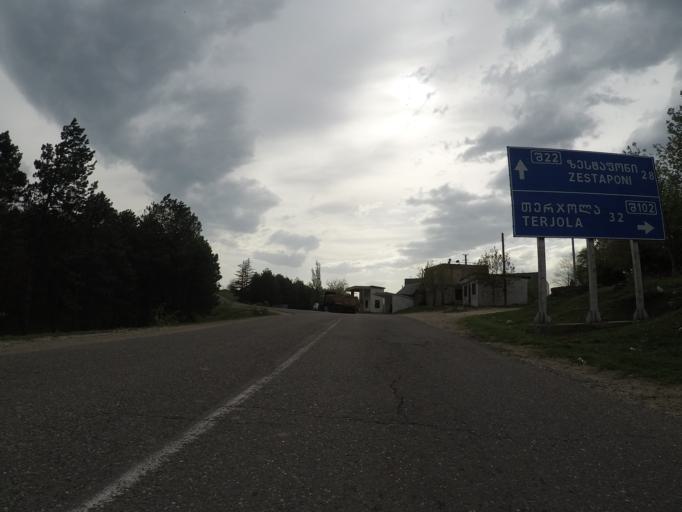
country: GE
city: Tqibuli
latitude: 42.2767
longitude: 43.2013
